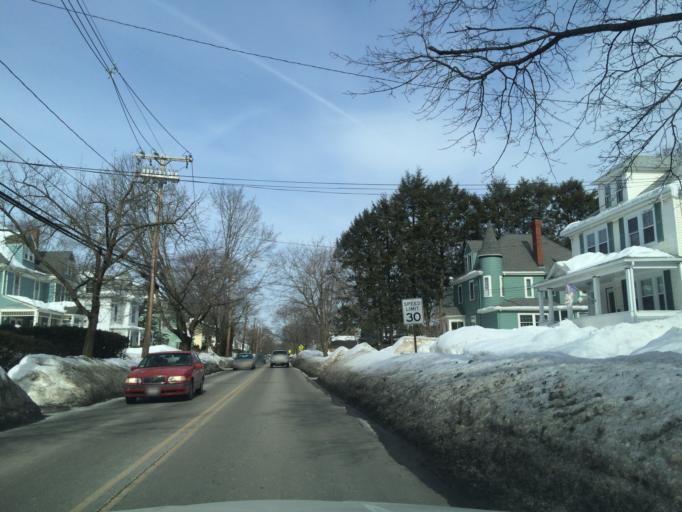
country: US
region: Massachusetts
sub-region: Middlesex County
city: Waltham
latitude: 42.3502
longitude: -71.2469
